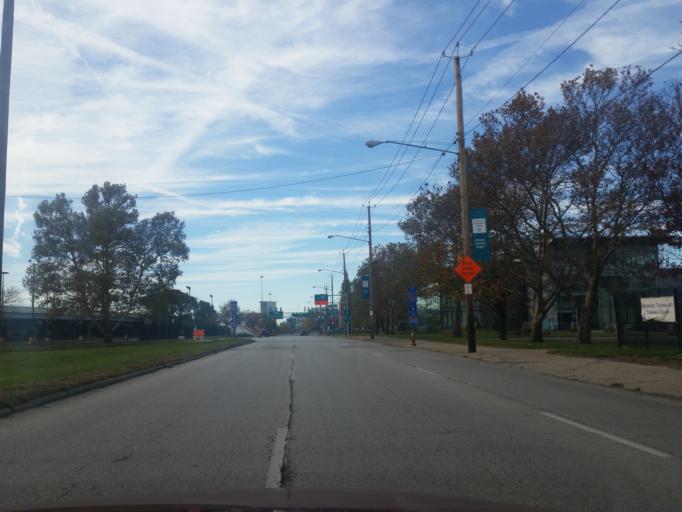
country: US
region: Ohio
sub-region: Cuyahoga County
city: Cleveland
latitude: 41.4909
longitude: -81.6657
